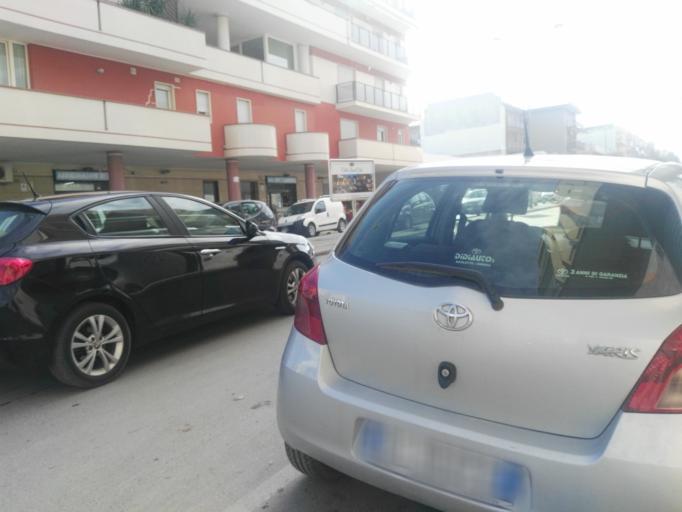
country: IT
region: Apulia
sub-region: Provincia di Barletta - Andria - Trani
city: Andria
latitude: 41.2228
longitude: 16.3065
